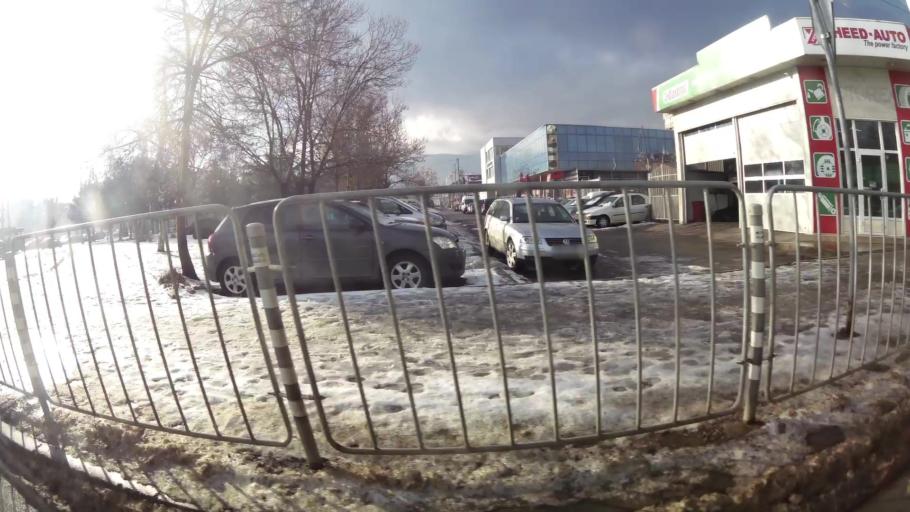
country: BG
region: Sofia-Capital
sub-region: Stolichna Obshtina
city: Sofia
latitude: 42.7005
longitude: 23.2966
